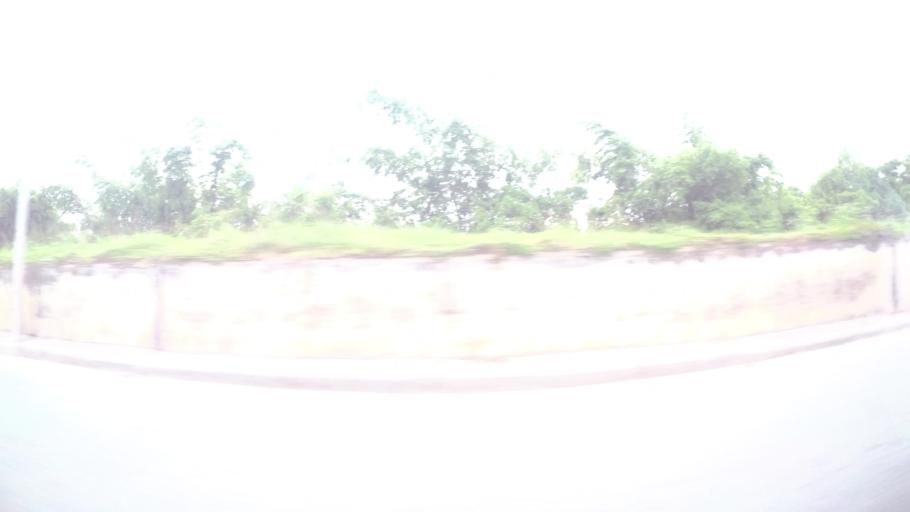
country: VN
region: Ha Noi
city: Trau Quy
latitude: 21.0564
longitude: 105.9190
